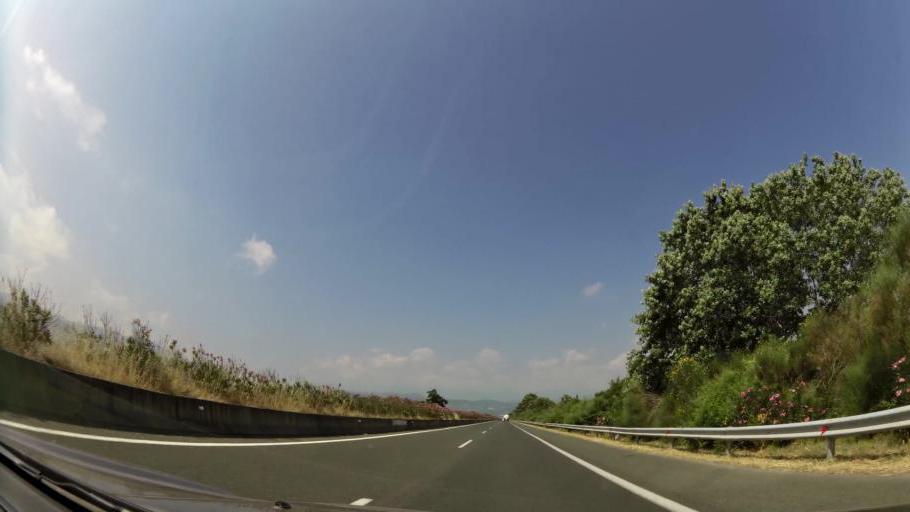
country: GR
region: Central Macedonia
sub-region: Nomos Imathias
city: Kouloura
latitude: 40.5340
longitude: 22.2984
